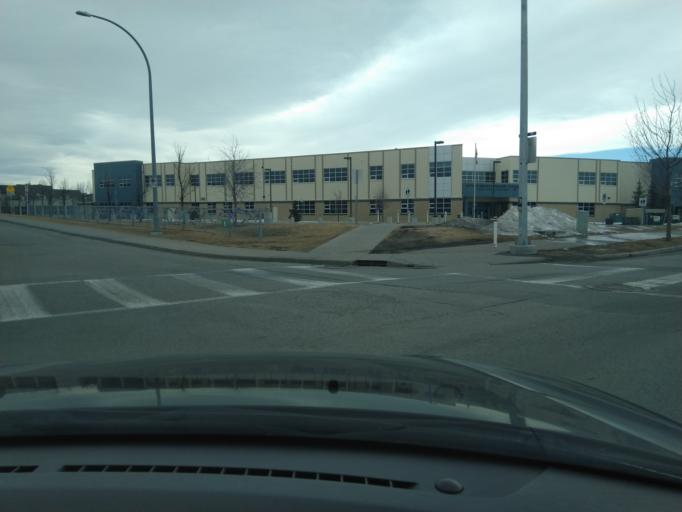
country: CA
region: Alberta
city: Calgary
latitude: 51.1633
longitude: -114.0881
